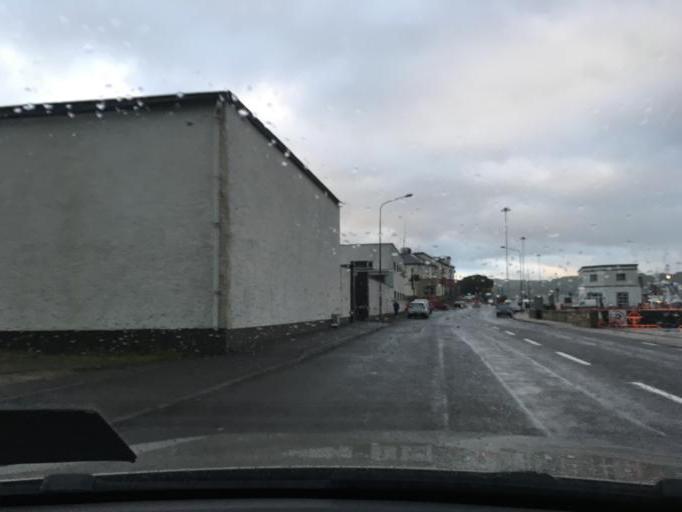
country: IE
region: Ulster
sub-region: County Donegal
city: Killybegs
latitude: 54.6360
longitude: -8.4433
